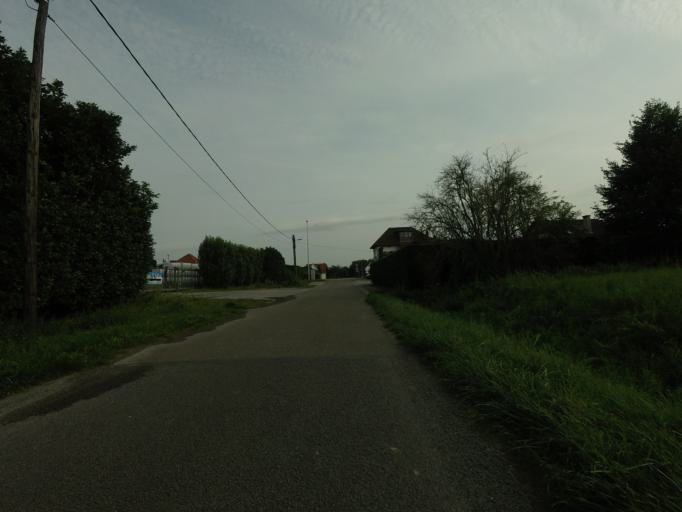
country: BE
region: Flanders
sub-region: Provincie Vlaams-Brabant
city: Kampenhout
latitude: 50.9326
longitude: 4.5347
